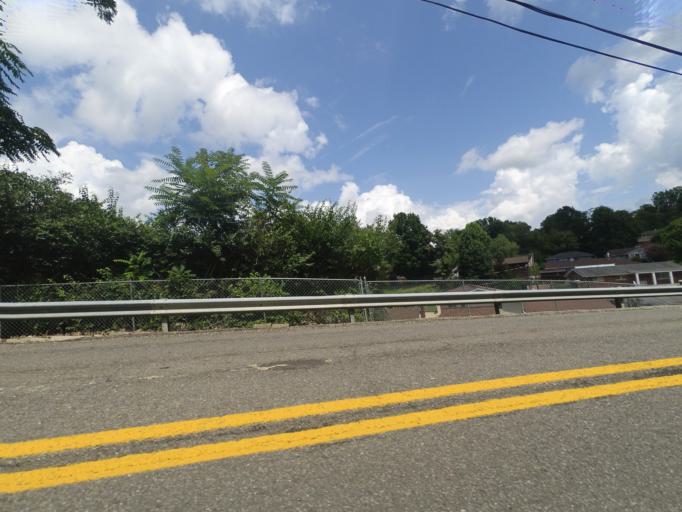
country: US
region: West Virginia
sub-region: Cabell County
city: Pea Ridge
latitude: 38.4030
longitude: -82.3816
